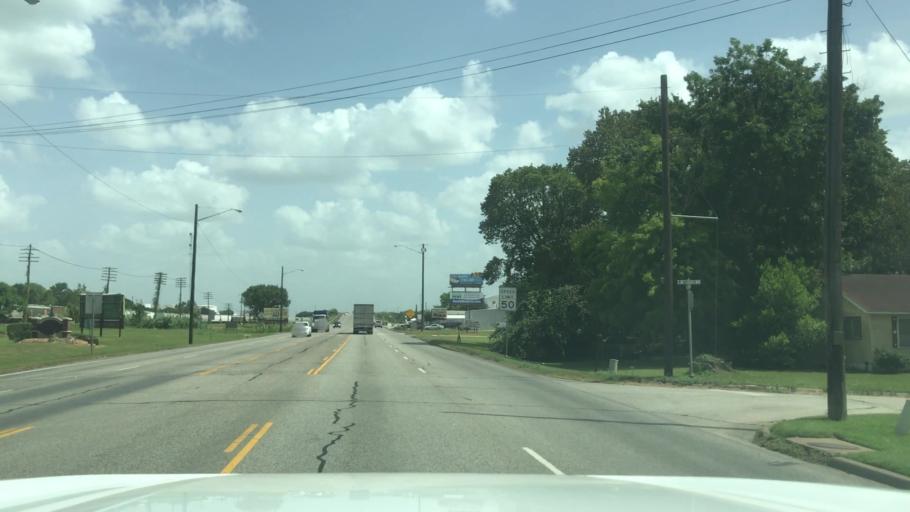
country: US
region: Texas
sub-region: Robertson County
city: Hearne
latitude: 30.8728
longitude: -96.5887
